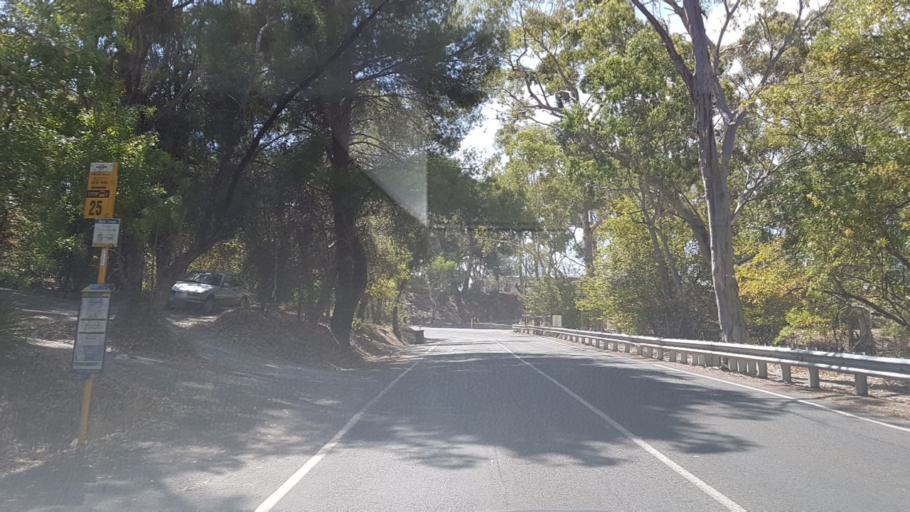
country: AU
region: South Australia
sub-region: Mitcham
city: Belair
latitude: -34.9994
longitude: 138.6325
